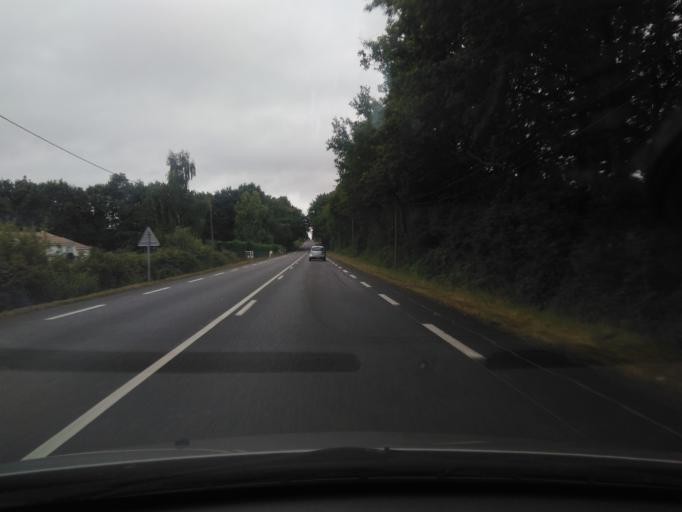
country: FR
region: Pays de la Loire
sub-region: Departement de la Vendee
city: Saint-Florent-des-Bois
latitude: 46.6177
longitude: -1.3591
